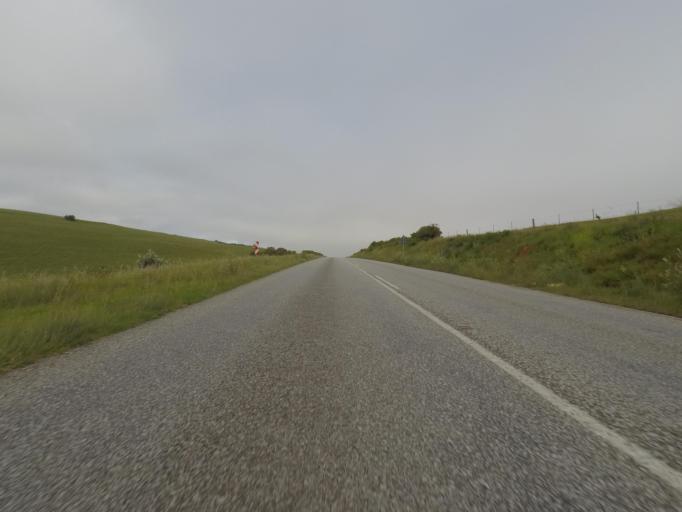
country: ZA
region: Eastern Cape
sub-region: Cacadu District Municipality
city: Port Alfred
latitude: -33.6077
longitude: 26.8192
